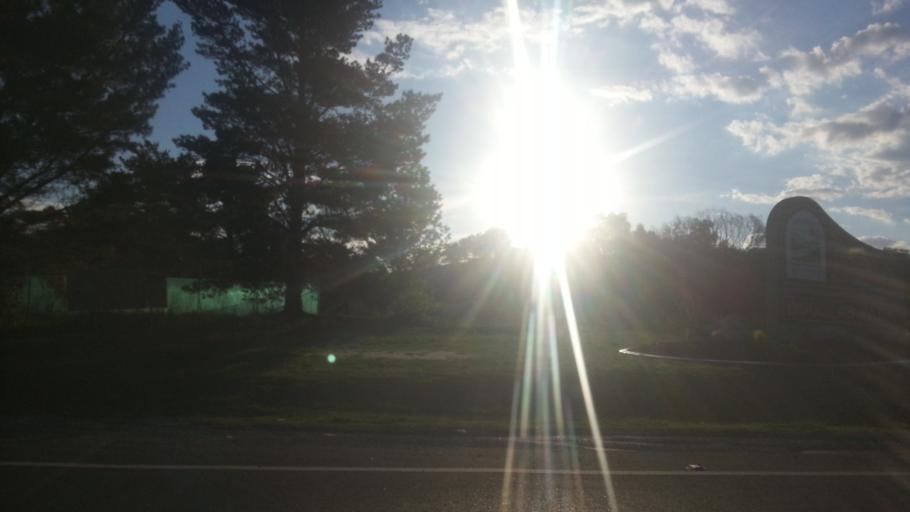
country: AU
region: New South Wales
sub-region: Wollondilly
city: Douglas Park
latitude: -34.1697
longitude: 150.7136
